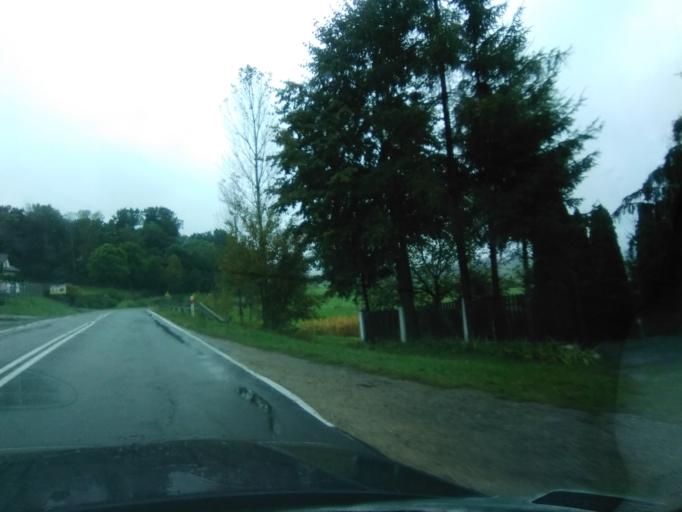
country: PL
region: Subcarpathian Voivodeship
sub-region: Powiat ropczycko-sedziszowski
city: Niedzwiada
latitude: 49.9919
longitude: 21.5638
